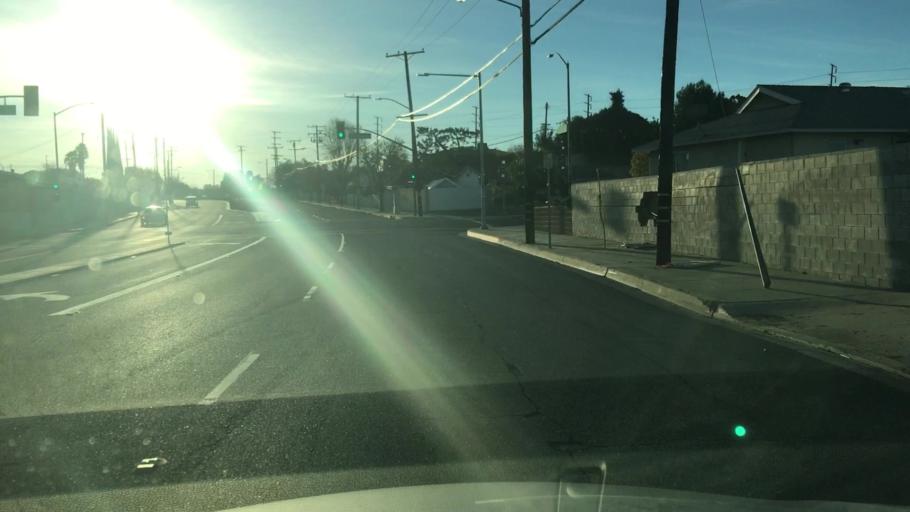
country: US
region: California
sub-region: Los Angeles County
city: East La Mirada
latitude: 33.9261
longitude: -117.9819
